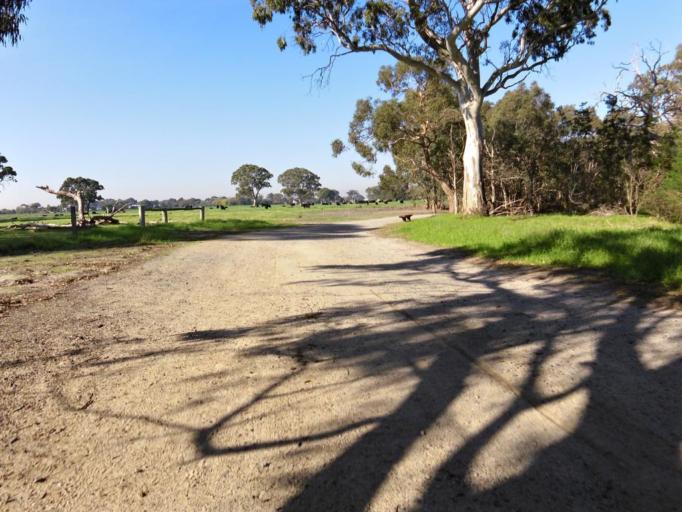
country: AU
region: Victoria
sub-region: Kingston
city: Waterways
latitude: -38.0039
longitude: 145.1324
